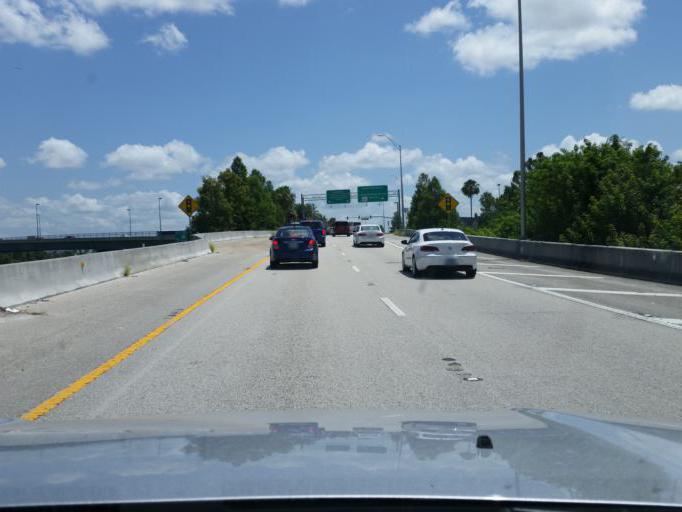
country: US
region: Florida
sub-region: Orange County
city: Tangelo Park
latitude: 28.4641
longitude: -81.4663
